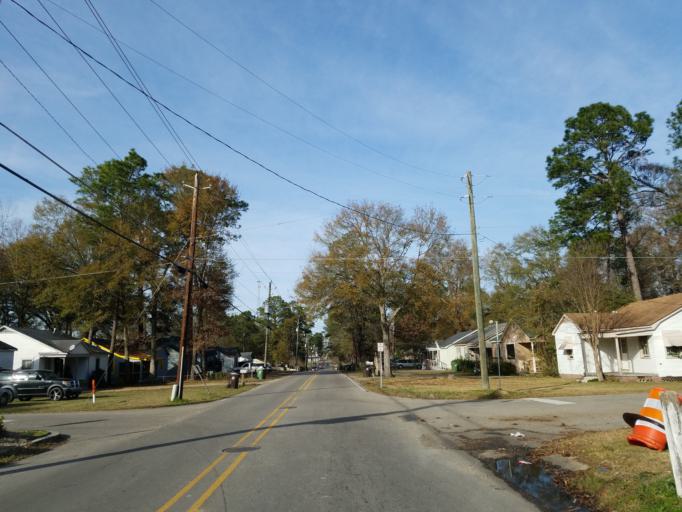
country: US
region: Mississippi
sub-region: Forrest County
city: Hattiesburg
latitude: 31.3283
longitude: -89.3278
